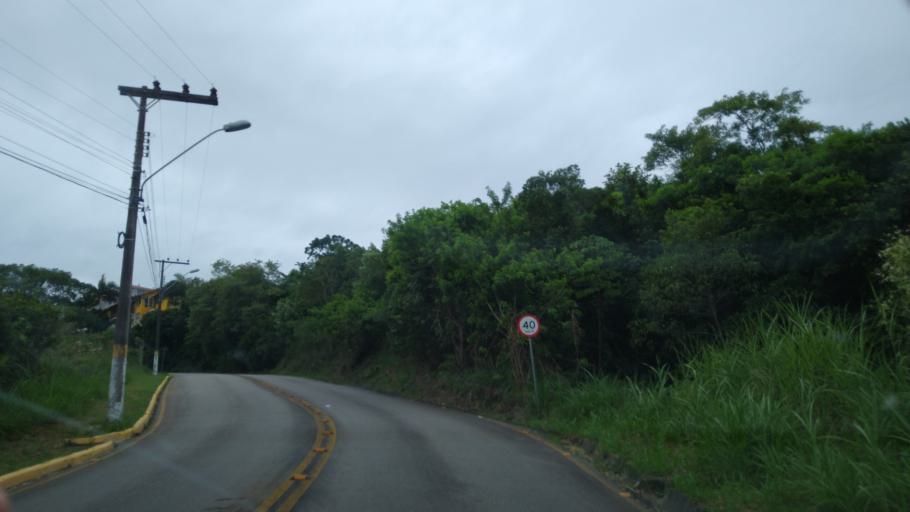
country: BR
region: Santa Catarina
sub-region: Itapema
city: Itapema
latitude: -27.0896
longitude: -48.6024
